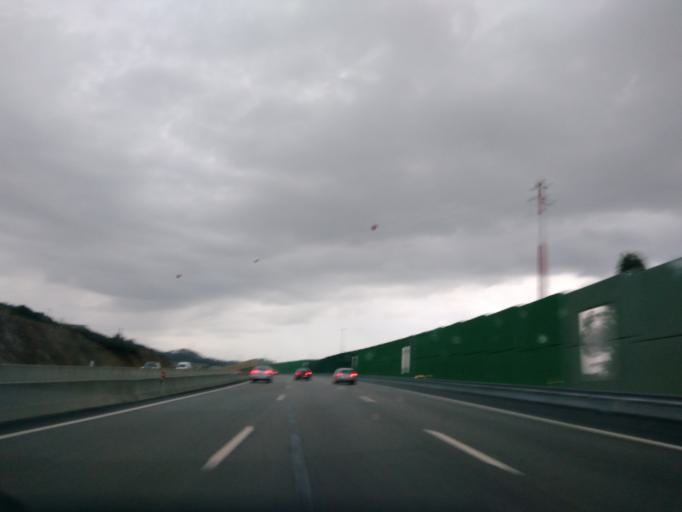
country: PT
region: Porto
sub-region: Trofa
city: Sao Romao do Coronado
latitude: 41.2939
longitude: -8.5418
